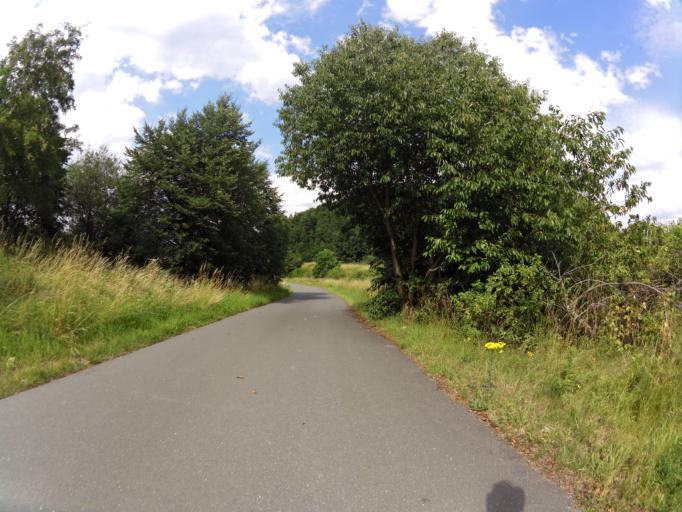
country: DE
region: Thuringia
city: Gorkwitz
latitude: 50.5673
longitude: 11.7757
